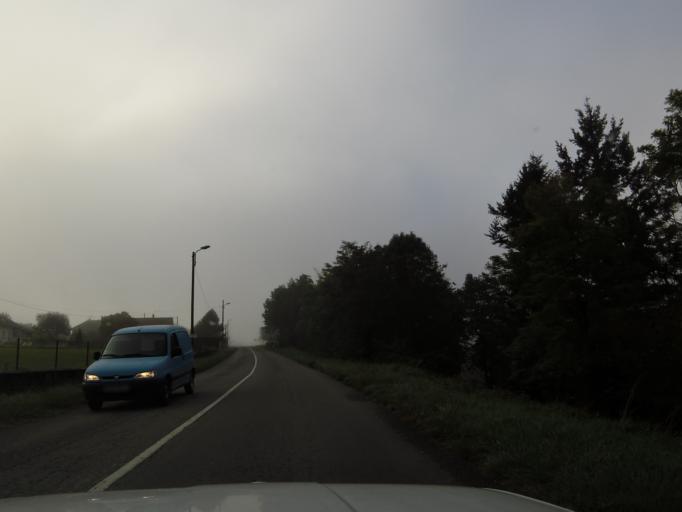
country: FR
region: Rhone-Alpes
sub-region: Departement de l'Isere
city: Creys-Mepieu
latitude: 45.7811
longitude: 5.4692
